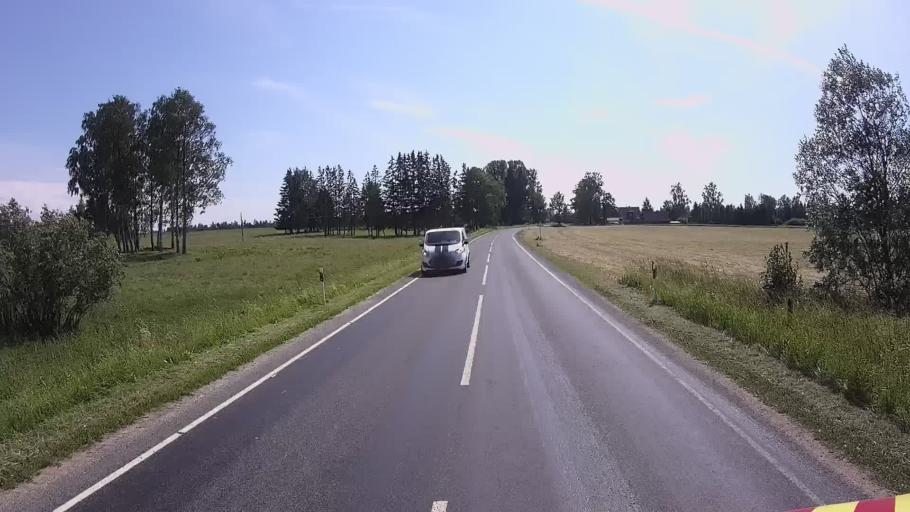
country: EE
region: Viljandimaa
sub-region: Karksi vald
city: Karksi-Nuia
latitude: 58.0598
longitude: 25.5507
